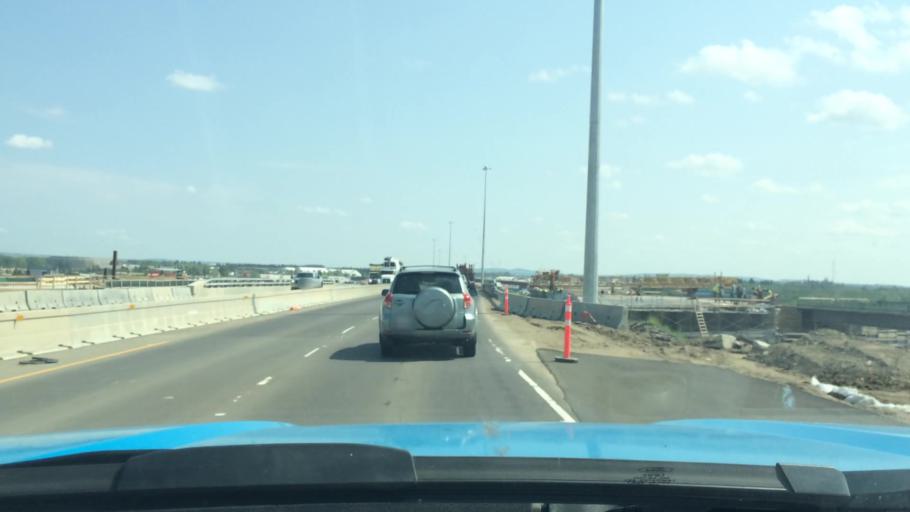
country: CA
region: Alberta
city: Red Deer
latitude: 52.2329
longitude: -113.8237
